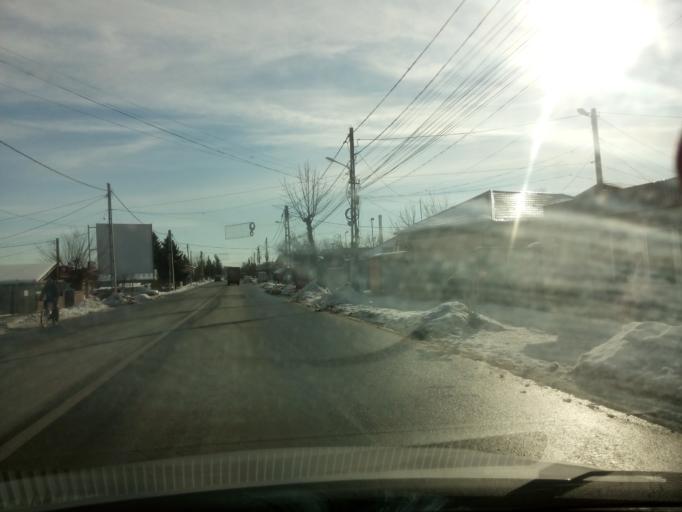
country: RO
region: Ilfov
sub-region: Comuna Popesti-Leordeni
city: Popesti-Leordeni
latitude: 44.3769
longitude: 26.1737
